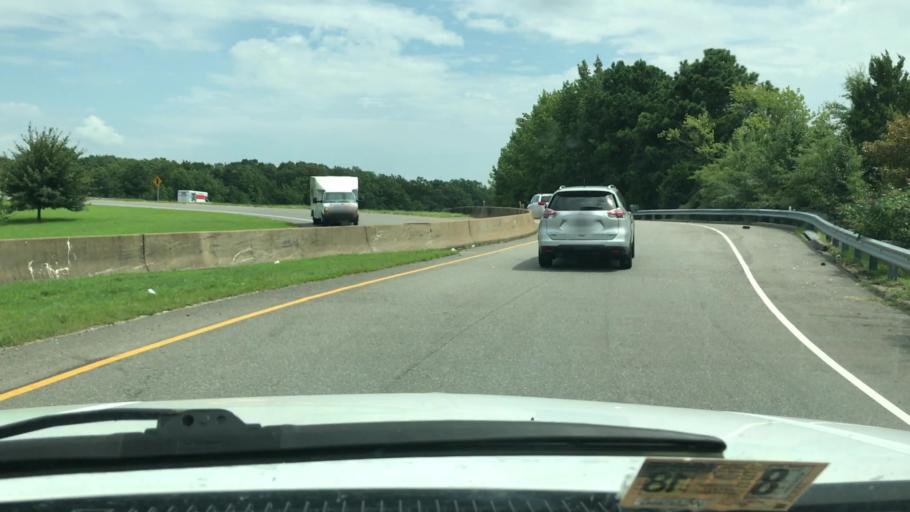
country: US
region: Virginia
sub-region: Chesterfield County
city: Bon Air
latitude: 37.5009
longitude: -77.5260
